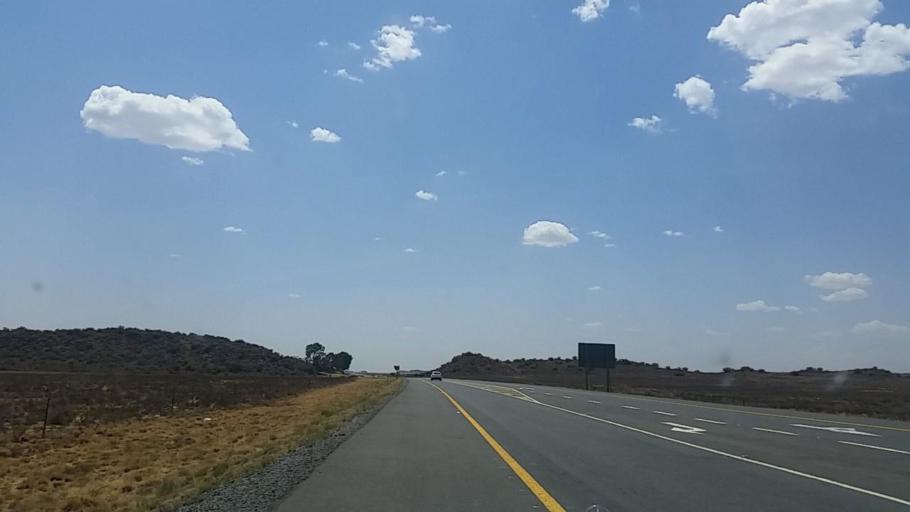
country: ZA
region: Northern Cape
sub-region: Pixley ka Seme District Municipality
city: Colesberg
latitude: -30.9538
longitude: 25.0301
